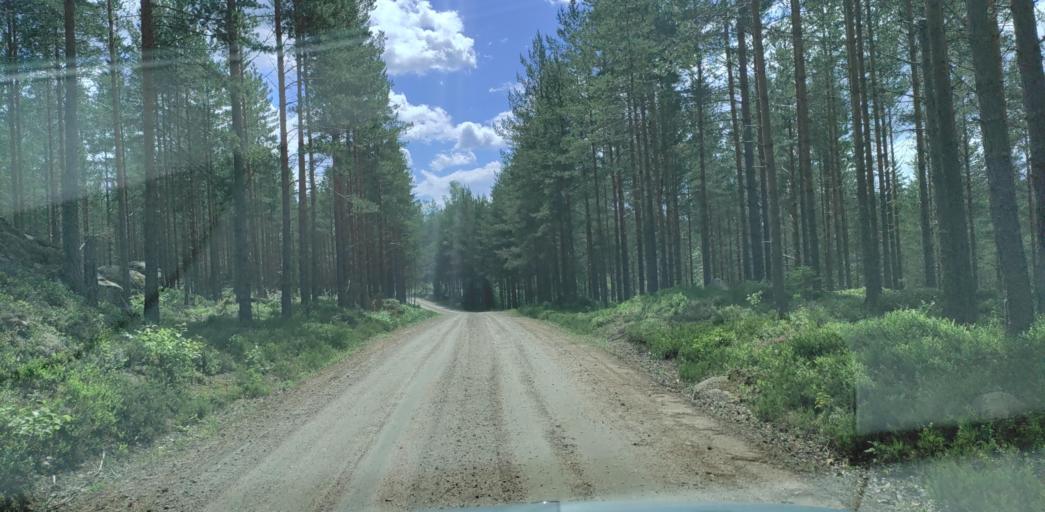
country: SE
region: Vaermland
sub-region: Hagfors Kommun
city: Ekshaerad
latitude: 60.0630
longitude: 13.2902
